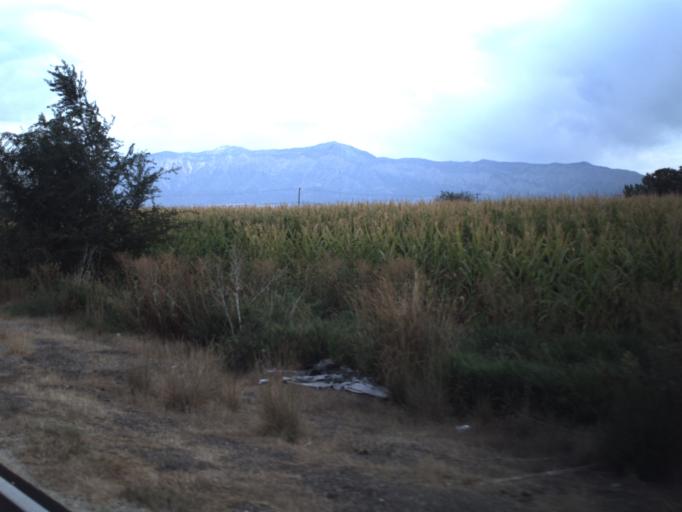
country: US
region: Utah
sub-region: Weber County
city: West Haven
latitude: 41.2331
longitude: -112.0928
